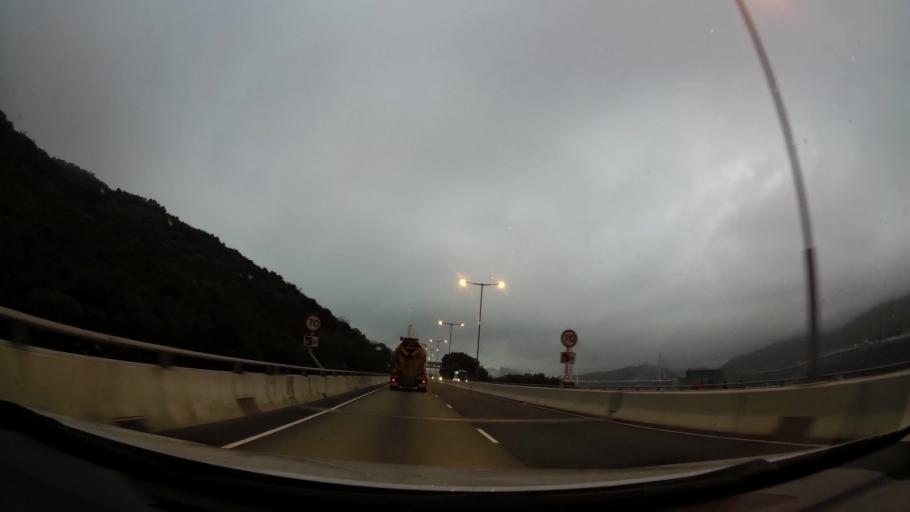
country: HK
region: Tsuen Wan
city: Tsuen Wan
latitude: 22.3603
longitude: 114.0908
